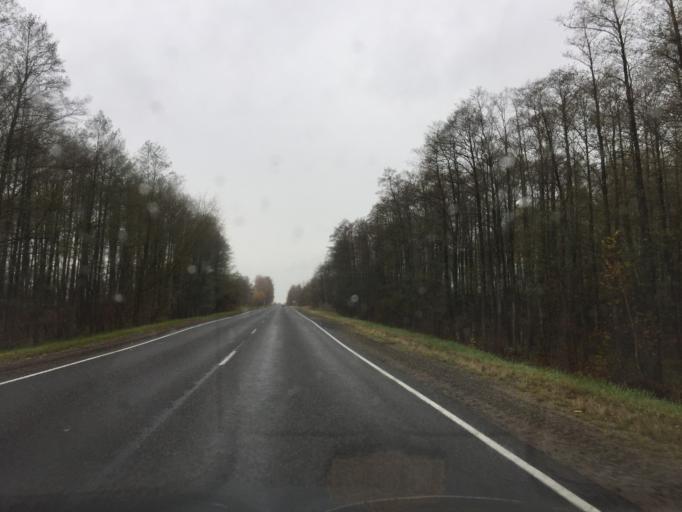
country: BY
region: Mogilev
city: Slawharad
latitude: 53.3499
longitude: 30.8207
